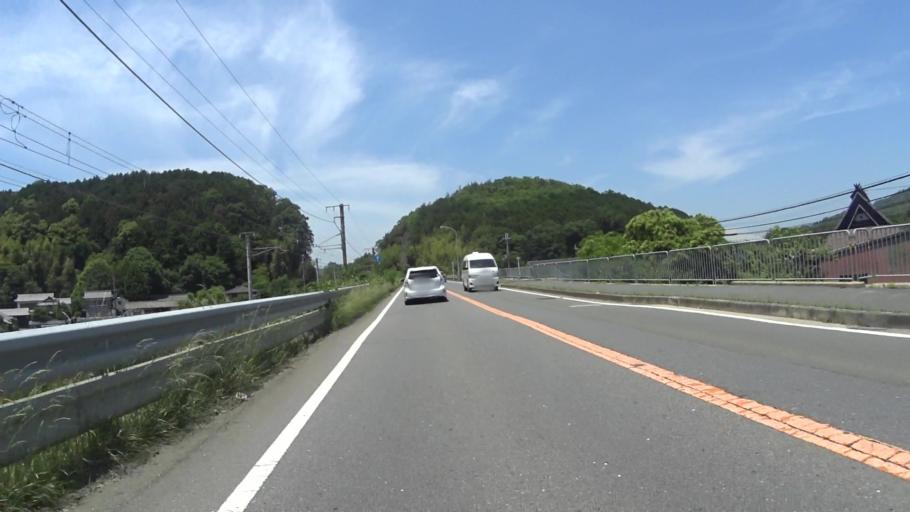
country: JP
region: Kyoto
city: Kameoka
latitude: 35.0796
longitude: 135.5178
